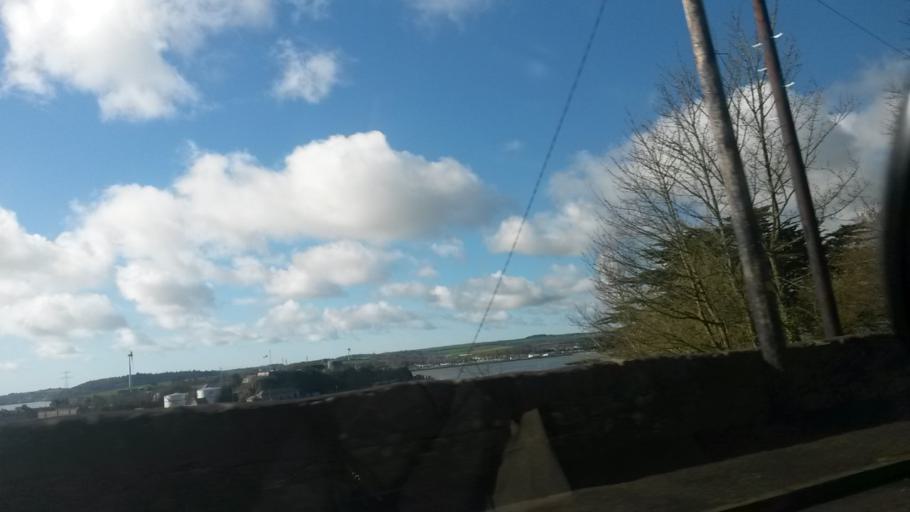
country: IE
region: Munster
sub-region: County Cork
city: Cobh
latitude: 51.8484
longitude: -8.3059
